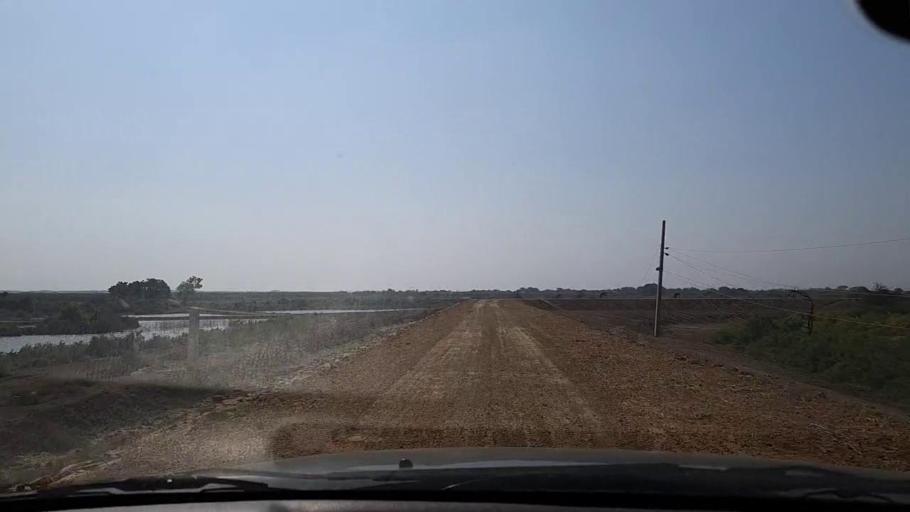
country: PK
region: Sindh
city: Chuhar Jamali
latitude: 24.4565
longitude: 67.8766
